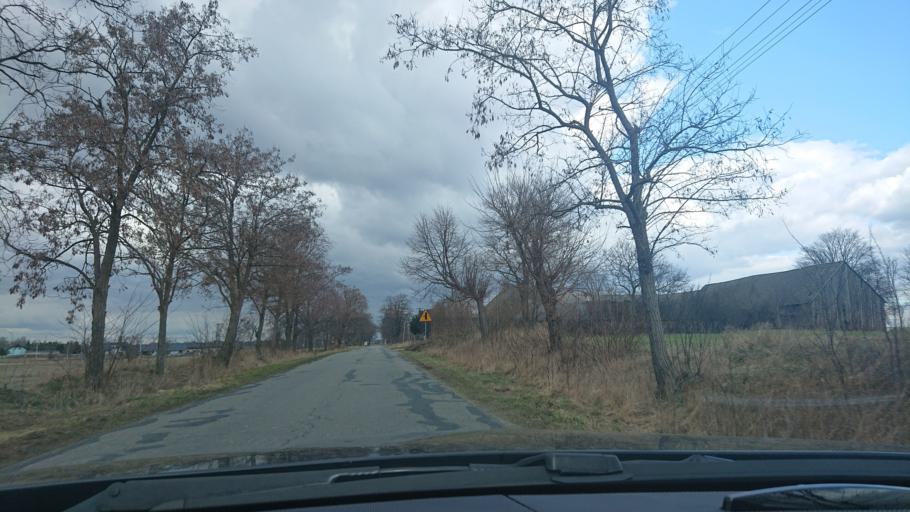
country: PL
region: Greater Poland Voivodeship
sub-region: Powiat gnieznienski
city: Niechanowo
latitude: 52.5712
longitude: 17.7038
